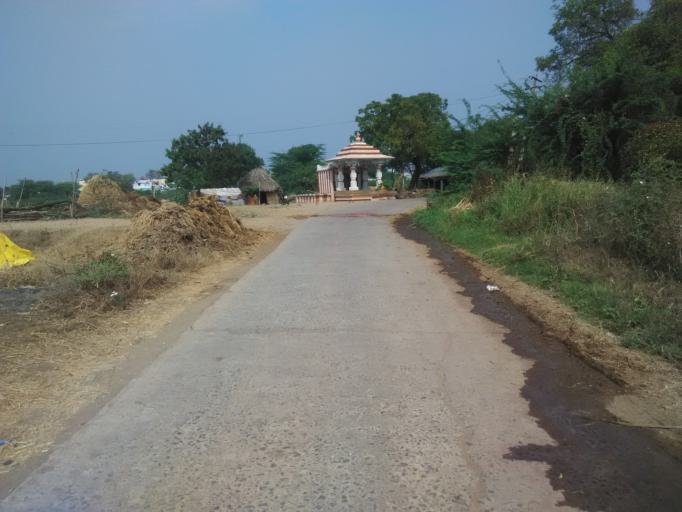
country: IN
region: Andhra Pradesh
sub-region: Kurnool
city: Nandyal
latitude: 15.4476
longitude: 78.4219
